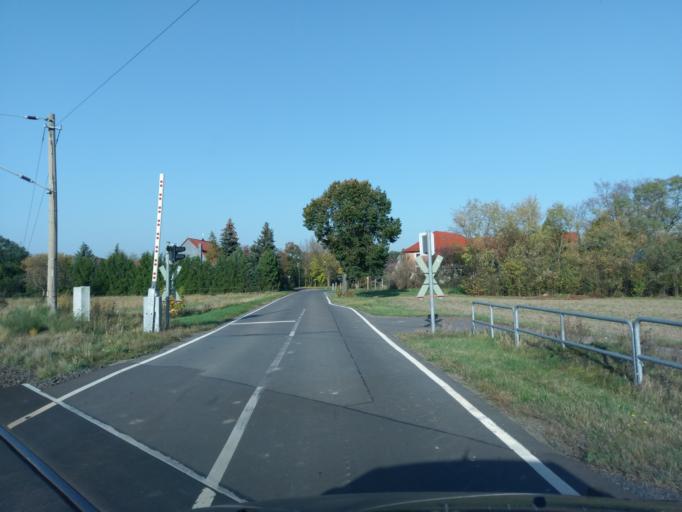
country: DE
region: Brandenburg
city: Muhlberg
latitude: 51.4991
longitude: 13.2813
